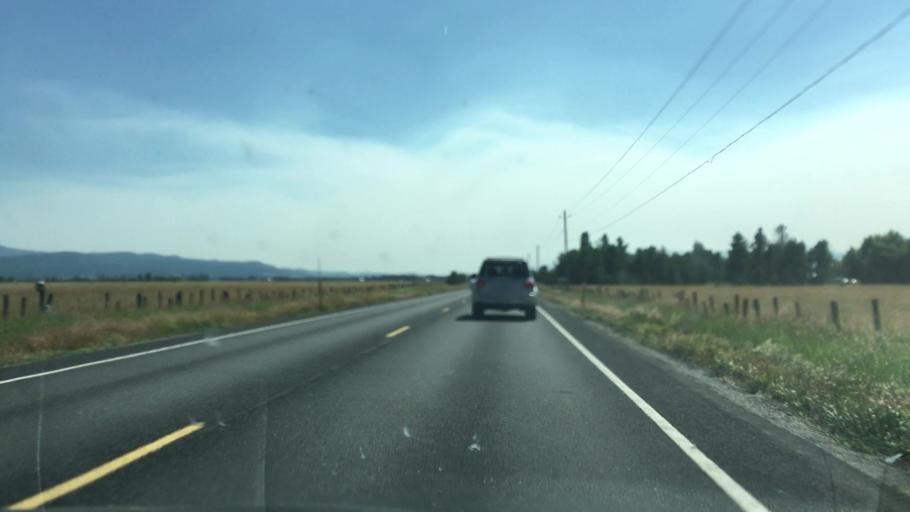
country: US
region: Idaho
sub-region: Valley County
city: McCall
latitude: 44.7591
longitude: -116.0783
